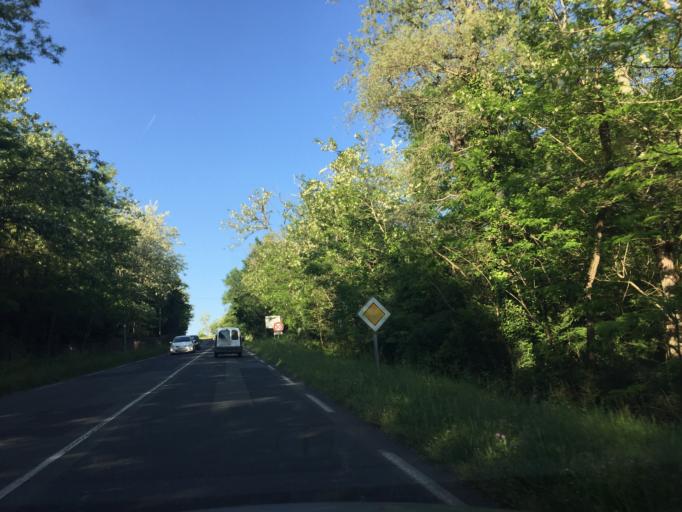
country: FR
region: Aquitaine
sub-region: Departement de la Dordogne
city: La Roche-Chalais
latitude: 45.1432
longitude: 0.0010
